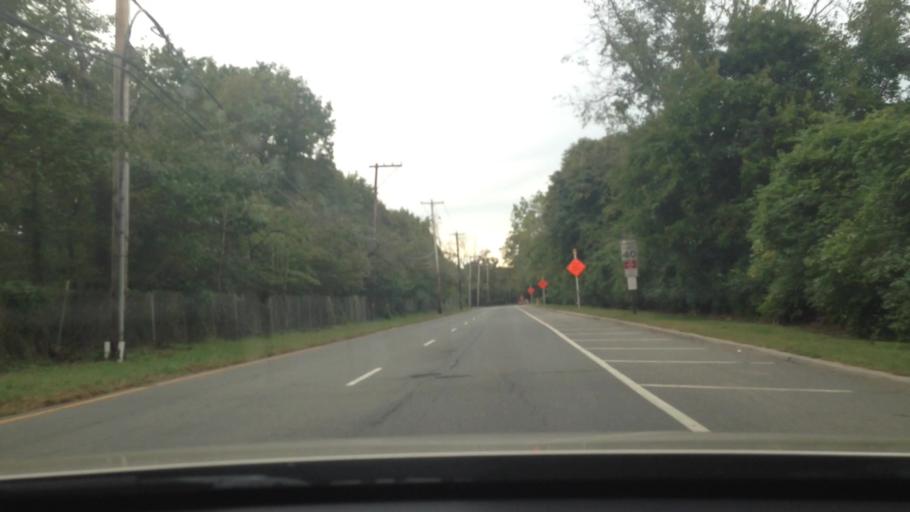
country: US
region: New York
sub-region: Nassau County
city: Old Westbury
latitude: 40.7809
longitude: -73.6088
